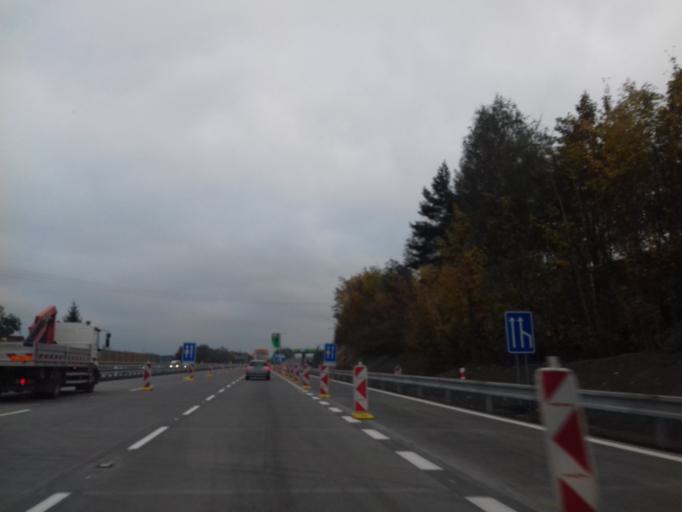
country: CZ
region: Central Bohemia
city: Ondrejov
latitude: 49.8412
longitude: 14.8098
